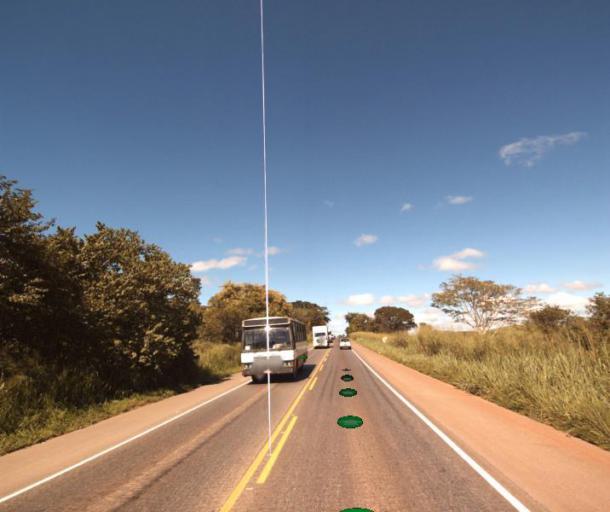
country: BR
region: Goias
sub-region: Rialma
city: Rialma
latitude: -15.2864
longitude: -49.5649
